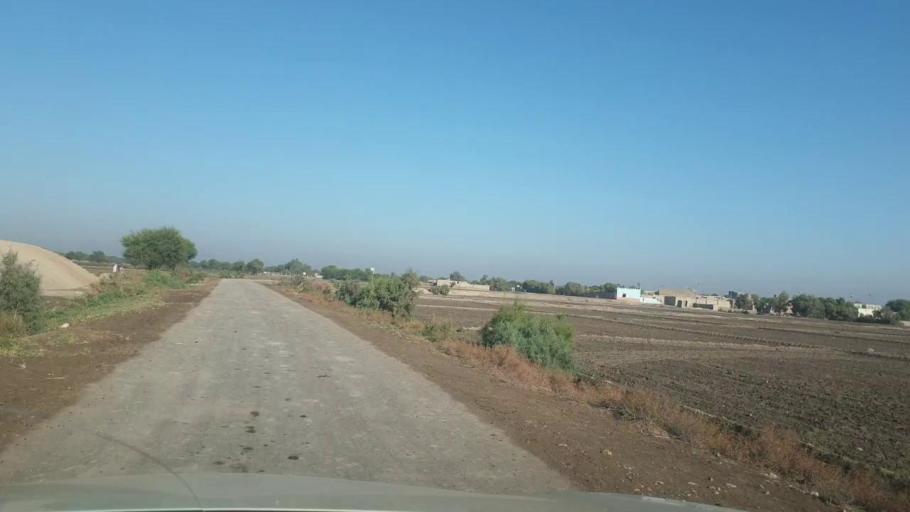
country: PK
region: Sindh
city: Bhan
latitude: 26.5331
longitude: 67.6742
